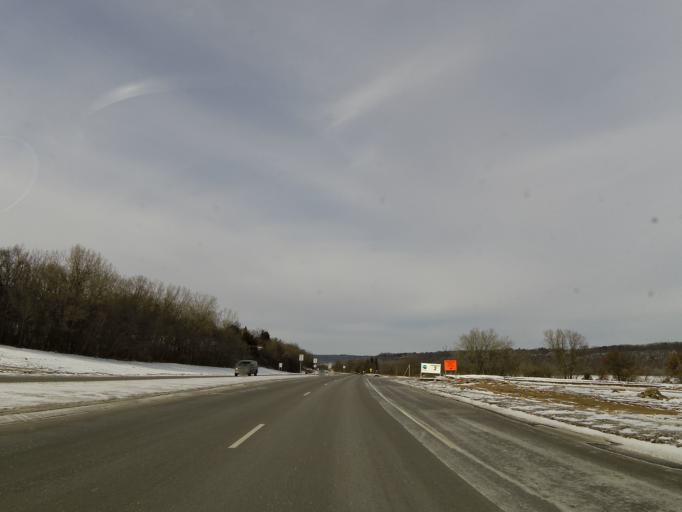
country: US
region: Minnesota
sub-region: Washington County
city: Oak Park Heights
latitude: 45.0384
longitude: -92.7944
